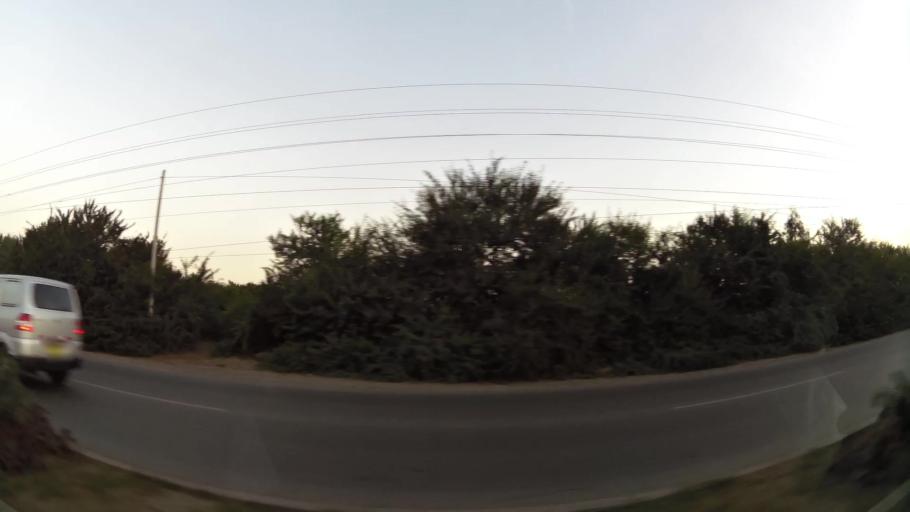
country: PE
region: Ica
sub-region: Provincia de Pisco
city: Villa Tupac Amaru
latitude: -13.7118
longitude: -76.1775
